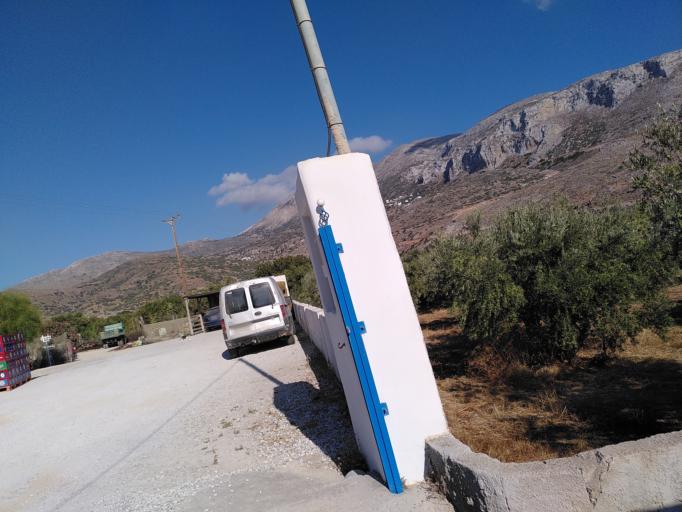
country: GR
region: South Aegean
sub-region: Nomos Kykladon
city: Amorgos
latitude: 36.9081
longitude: 25.9782
